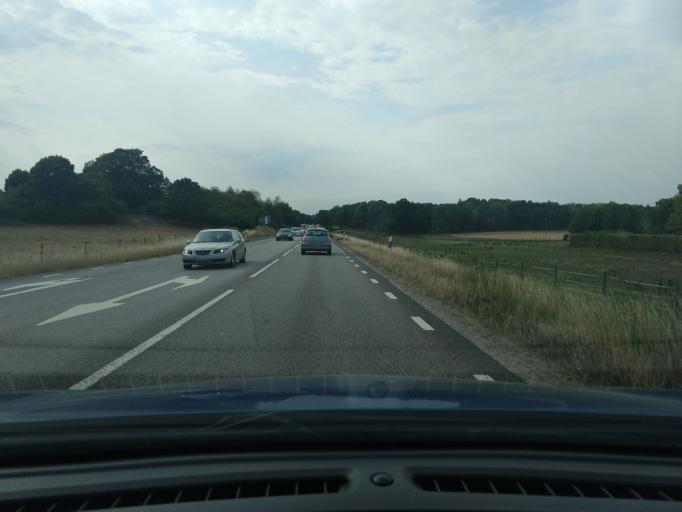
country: SE
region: Blekinge
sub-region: Karlskrona Kommun
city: Sturko
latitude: 56.1883
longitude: 15.7111
